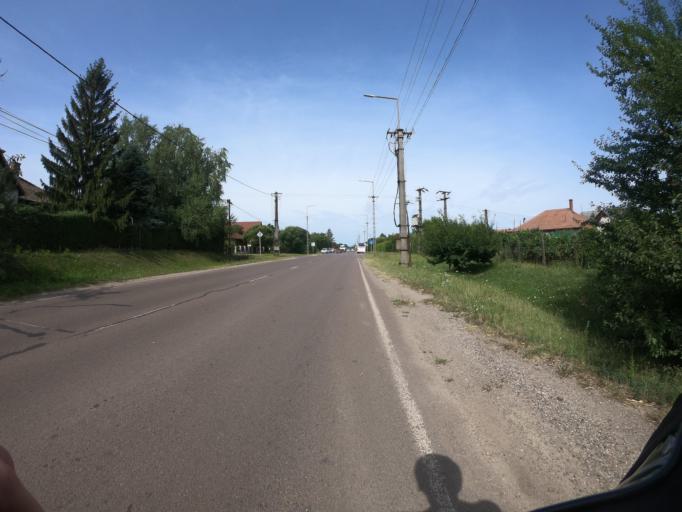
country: HU
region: Jasz-Nagykun-Szolnok
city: Tiszafured
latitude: 47.6064
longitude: 20.7707
